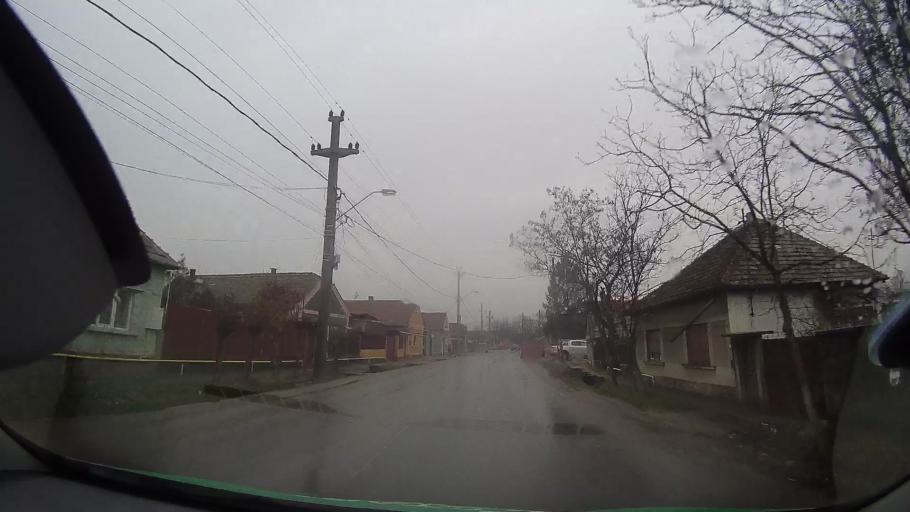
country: RO
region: Bihor
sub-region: Municipiul Salonta
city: Salonta
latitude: 46.7972
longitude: 21.6557
